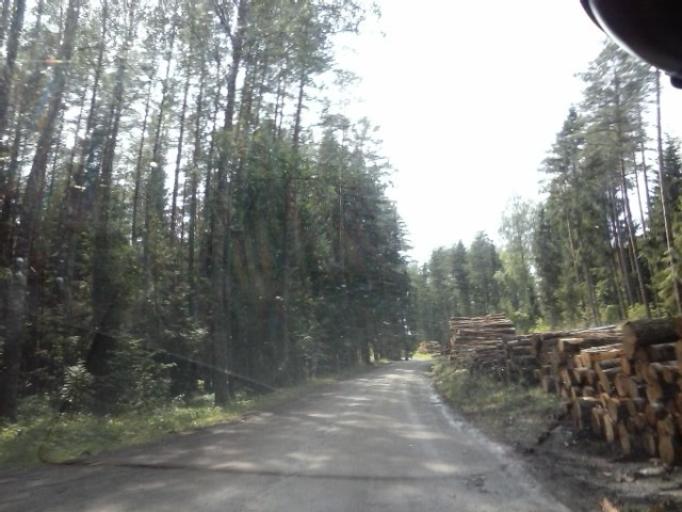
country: EE
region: Tartu
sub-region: UElenurme vald
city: Ulenurme
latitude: 58.2580
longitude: 26.9373
